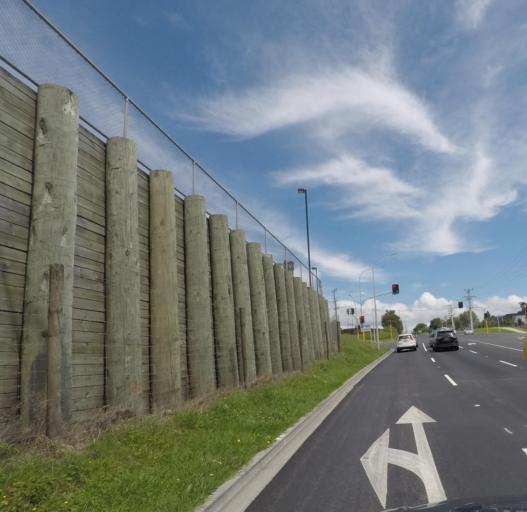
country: NZ
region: Auckland
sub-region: Auckland
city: Rothesay Bay
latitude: -36.6242
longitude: 174.6726
